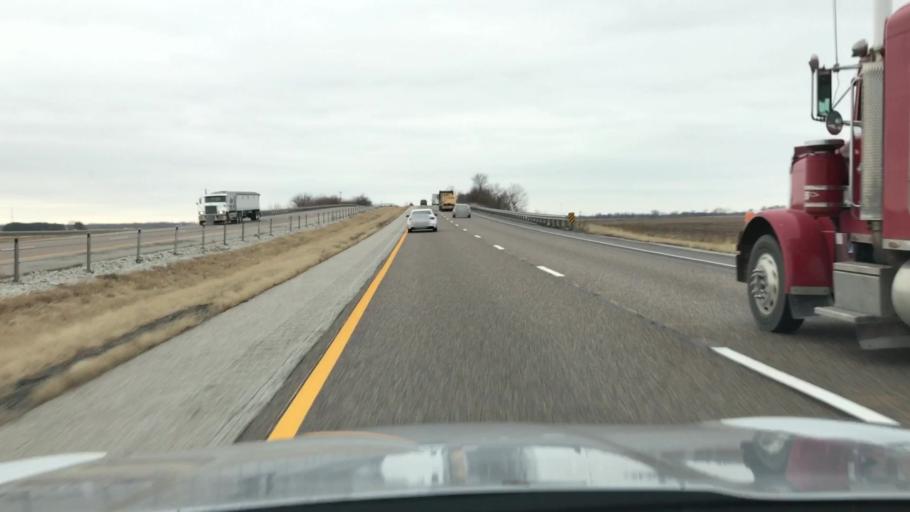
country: US
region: Illinois
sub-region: Madison County
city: Edwardsville
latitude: 38.8286
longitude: -89.8807
